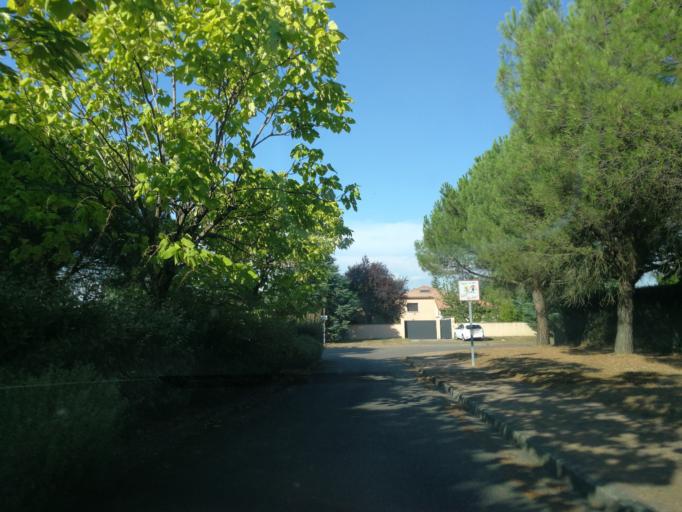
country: FR
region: Midi-Pyrenees
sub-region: Departement de la Haute-Garonne
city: Balma
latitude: 43.6191
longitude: 1.5172
